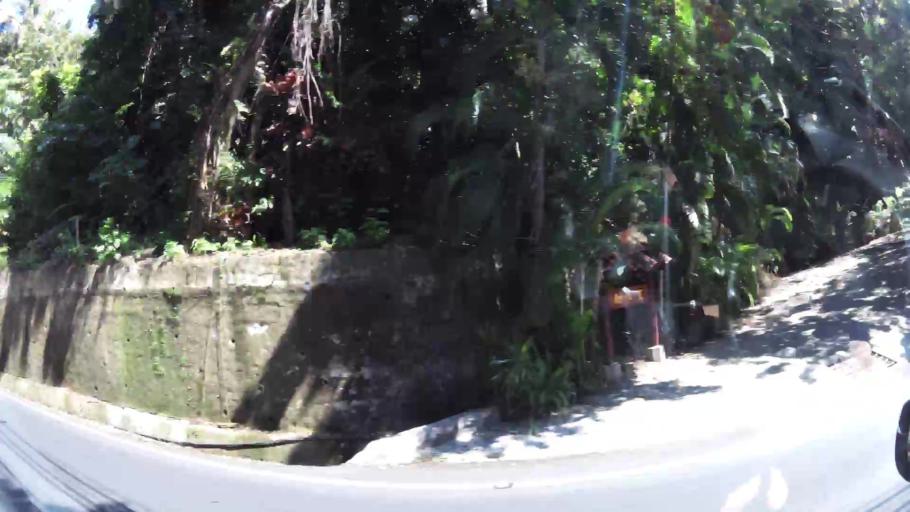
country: CR
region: Puntarenas
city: Quepos
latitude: 9.3970
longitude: -84.1544
